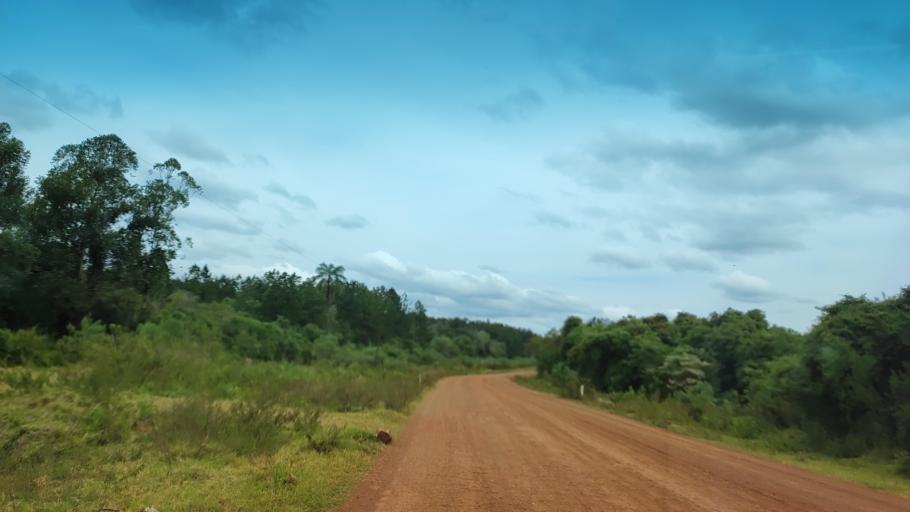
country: AR
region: Misiones
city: Garupa
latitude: -27.5035
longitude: -55.9702
